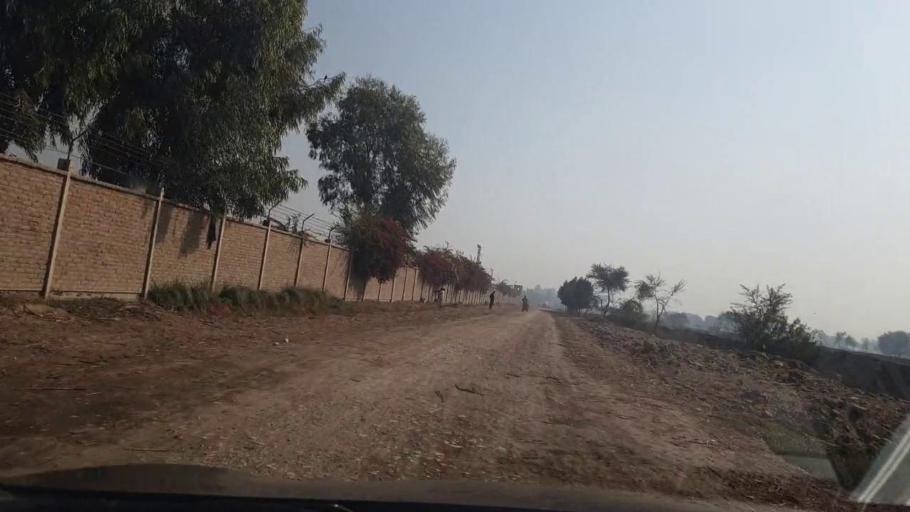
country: PK
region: Sindh
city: Ubauro
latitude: 28.1174
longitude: 69.7195
